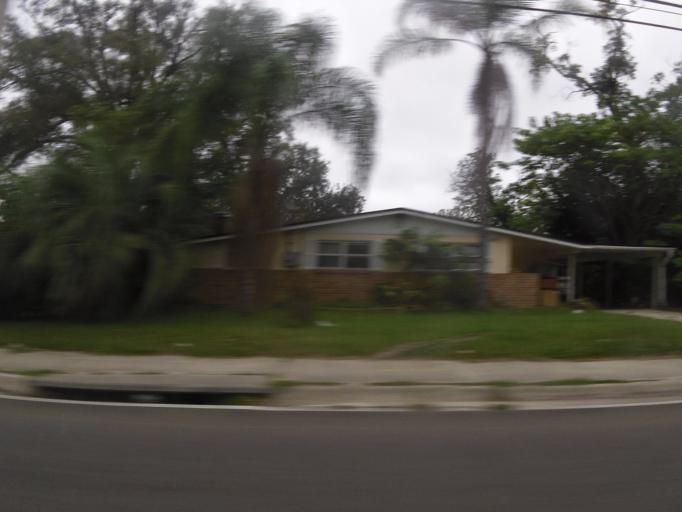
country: US
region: Florida
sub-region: Clay County
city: Bellair-Meadowbrook Terrace
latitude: 30.2703
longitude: -81.7501
